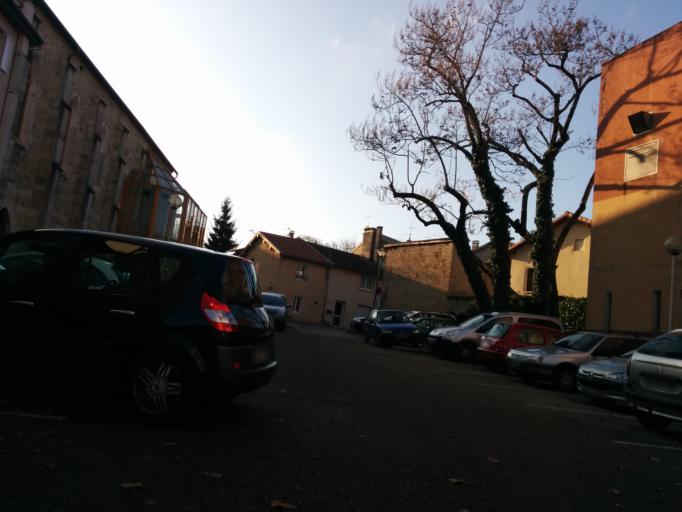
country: FR
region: Rhone-Alpes
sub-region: Departement de l'Ain
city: Meximieux
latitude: 45.9058
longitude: 5.1957
